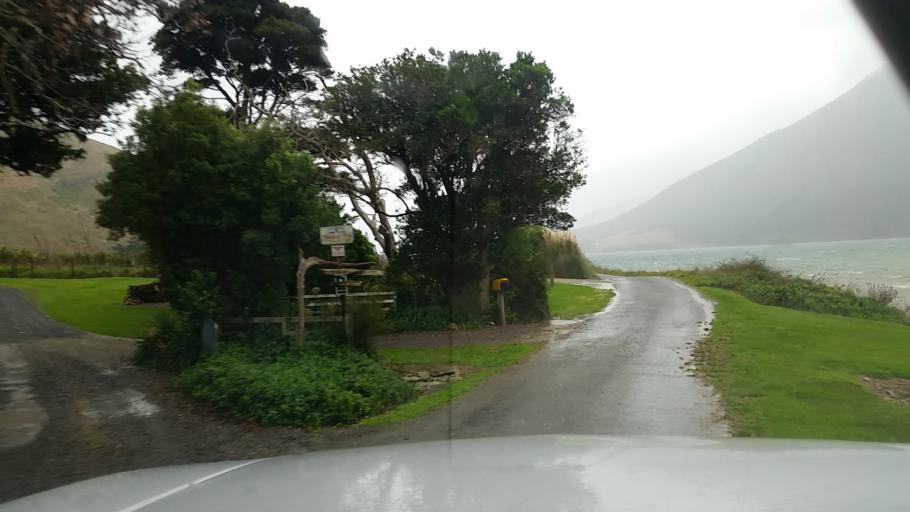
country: NZ
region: Marlborough
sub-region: Marlborough District
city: Picton
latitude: -41.1129
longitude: 174.0347
